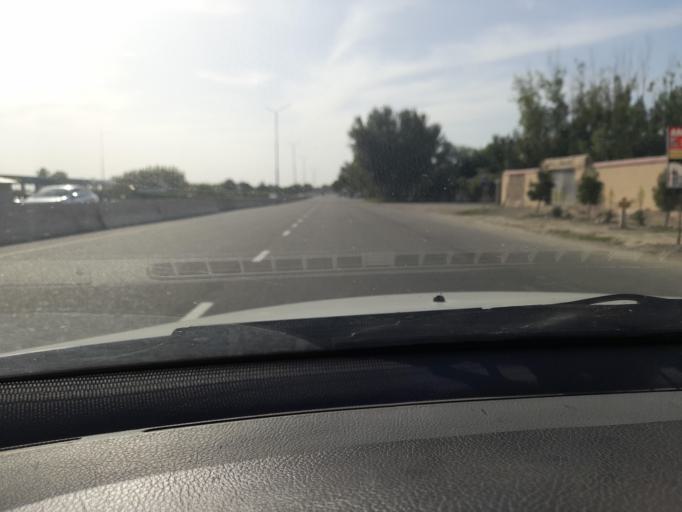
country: UZ
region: Samarqand
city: Kattaqo'rg'on
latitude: 39.9250
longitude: 66.2241
